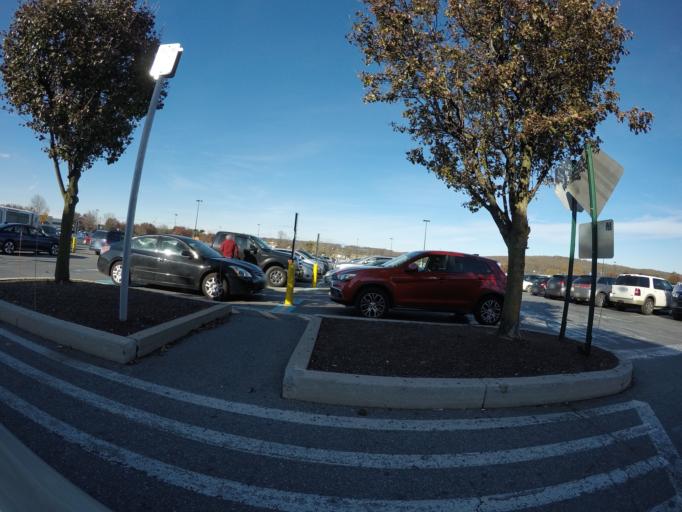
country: US
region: Pennsylvania
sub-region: Chester County
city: Parkesburg
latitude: 39.9805
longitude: -75.9341
